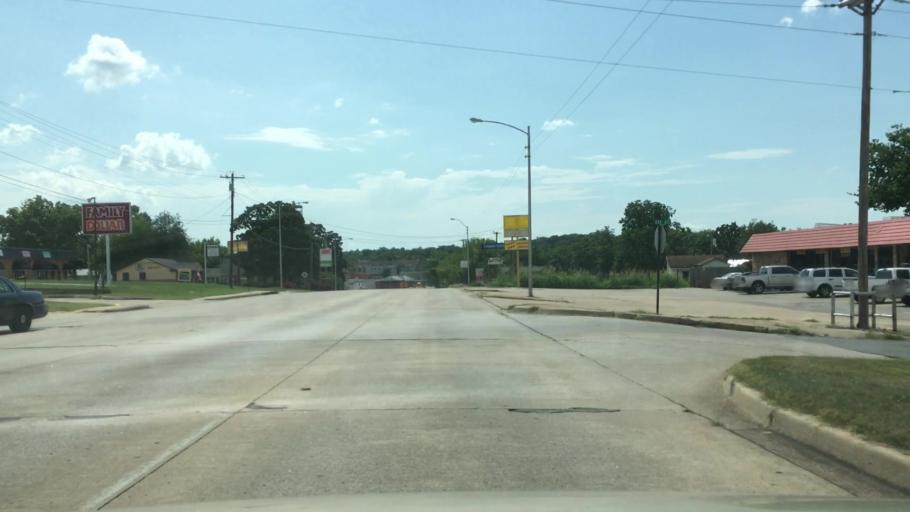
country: US
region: Oklahoma
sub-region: Cherokee County
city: Tahlequah
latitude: 35.9154
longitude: -94.9645
